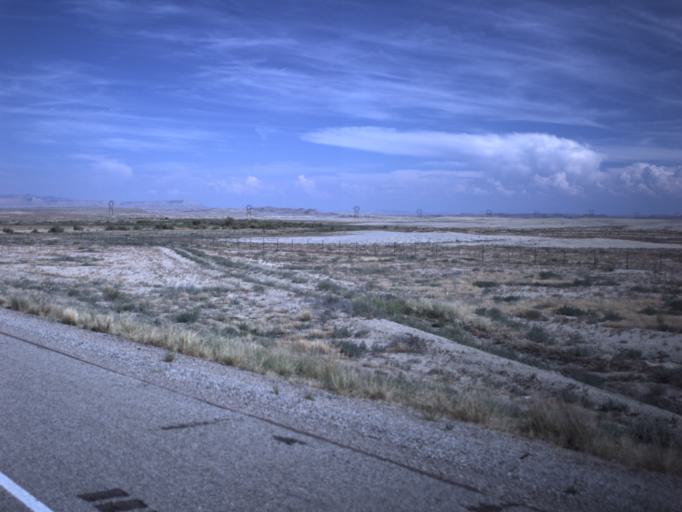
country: US
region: Utah
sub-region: Carbon County
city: East Carbon City
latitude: 38.9622
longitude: -110.2849
